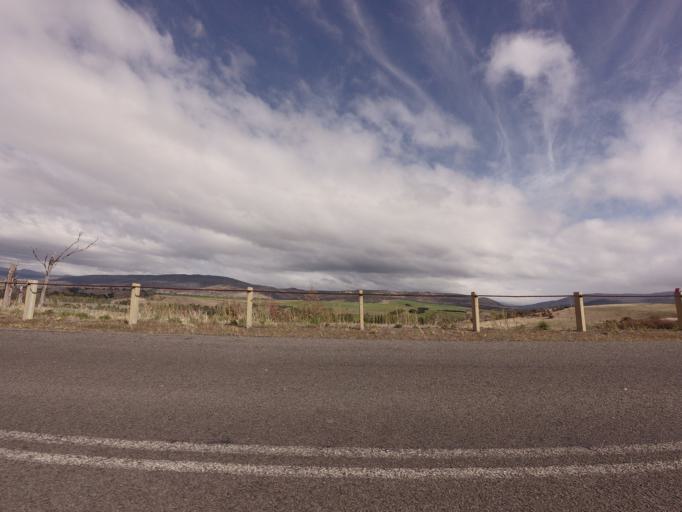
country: AU
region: Tasmania
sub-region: Derwent Valley
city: New Norfolk
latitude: -42.6916
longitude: 146.8781
